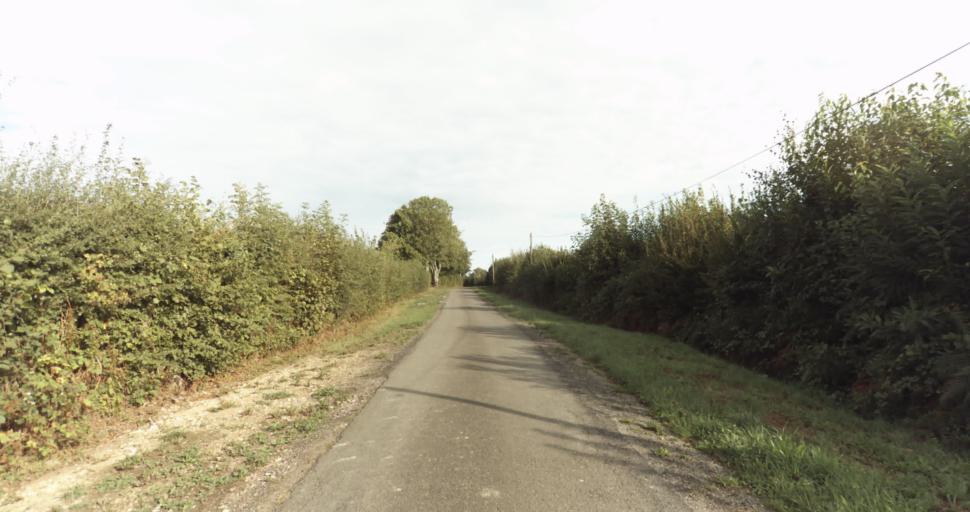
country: FR
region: Lower Normandy
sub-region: Departement de l'Orne
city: Gace
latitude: 48.8288
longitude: 0.2116
